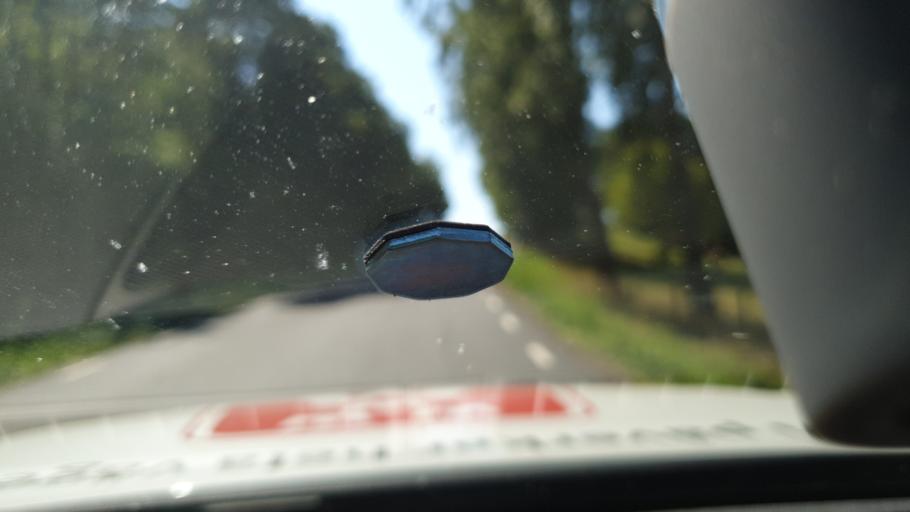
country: SE
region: Skane
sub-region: Sjobo Kommun
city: Blentarp
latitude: 55.5638
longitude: 13.5736
